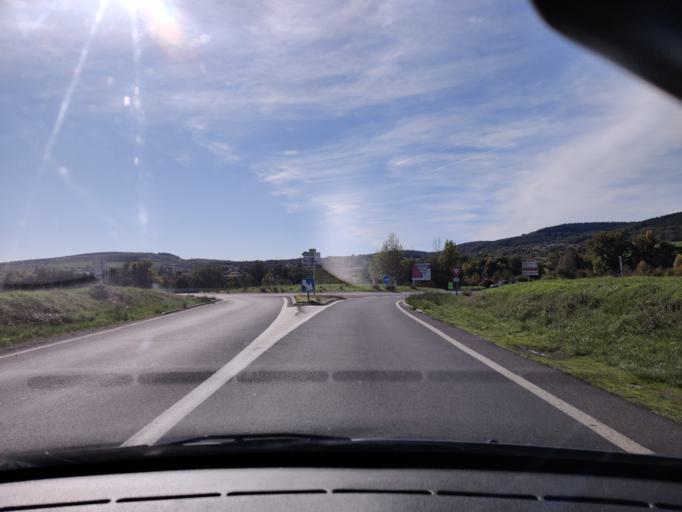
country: FR
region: Auvergne
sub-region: Departement du Puy-de-Dome
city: Combronde
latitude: 45.9937
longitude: 3.0900
